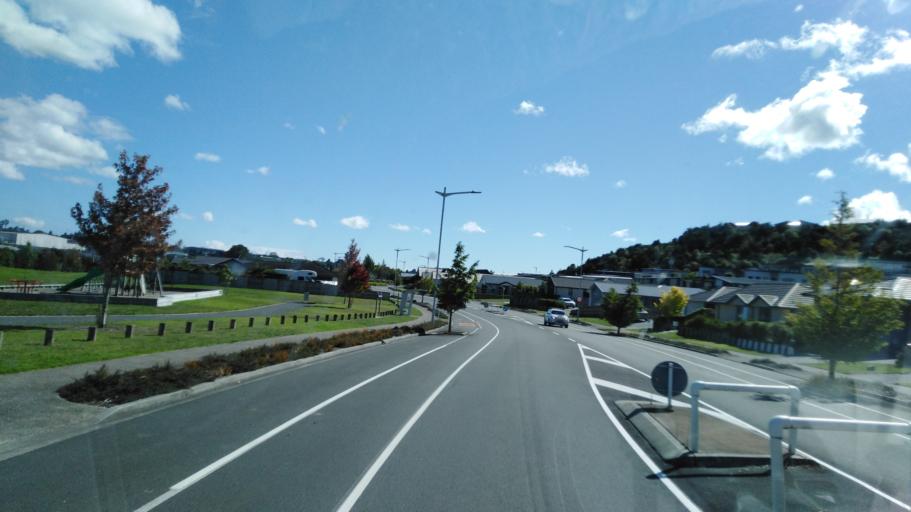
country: NZ
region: Bay of Plenty
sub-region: Tauranga City
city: Tauranga
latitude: -37.7561
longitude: 176.1039
